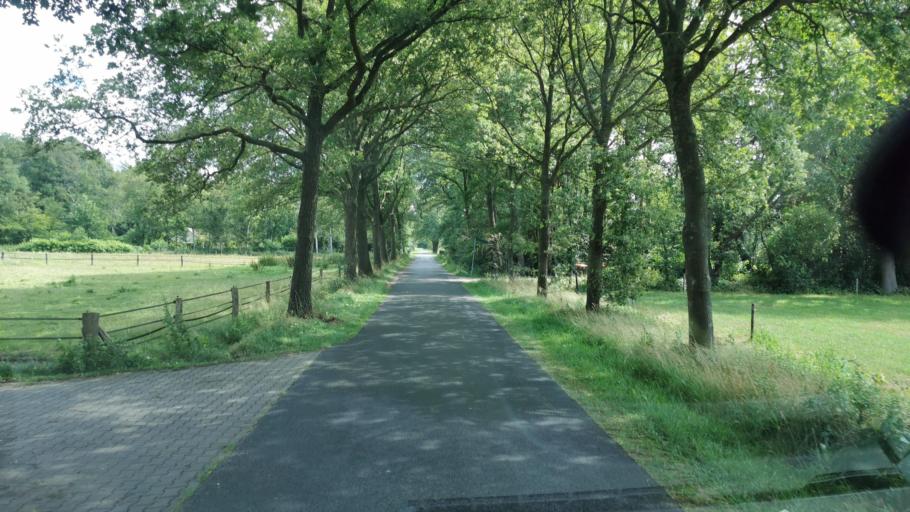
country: NL
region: Overijssel
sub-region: Gemeente Haaksbergen
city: Haaksbergen
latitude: 52.1330
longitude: 6.7345
